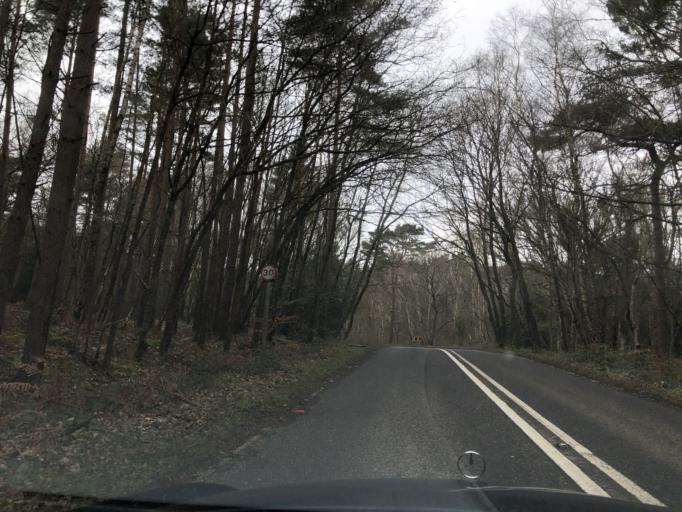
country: GB
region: England
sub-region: Surrey
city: Pirbright
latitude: 51.2969
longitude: -0.6829
